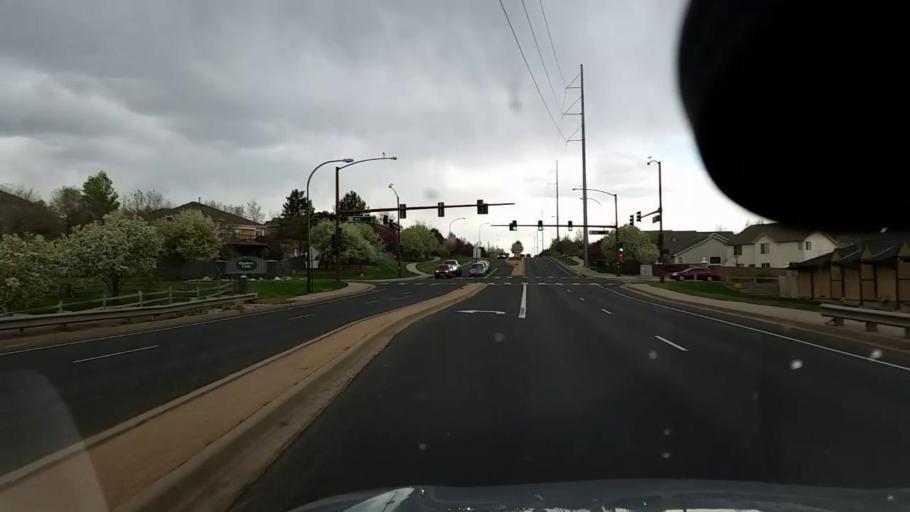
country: US
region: Colorado
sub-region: Adams County
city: Northglenn
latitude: 39.9411
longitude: -104.9782
